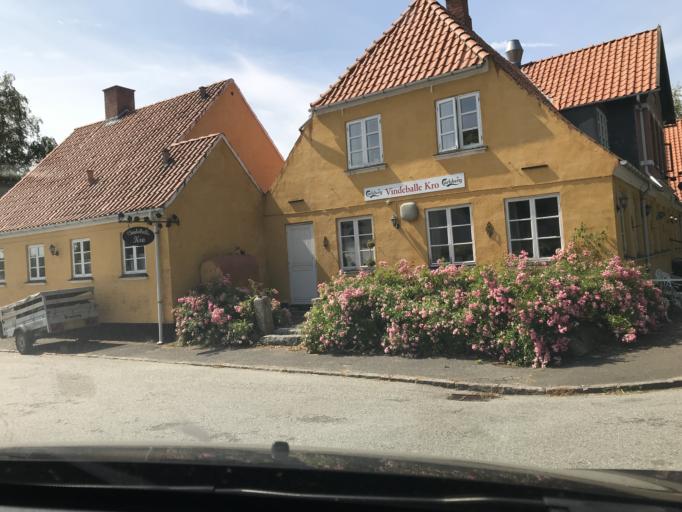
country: DK
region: South Denmark
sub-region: AEro Kommune
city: AEroskobing
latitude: 54.8729
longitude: 10.3568
